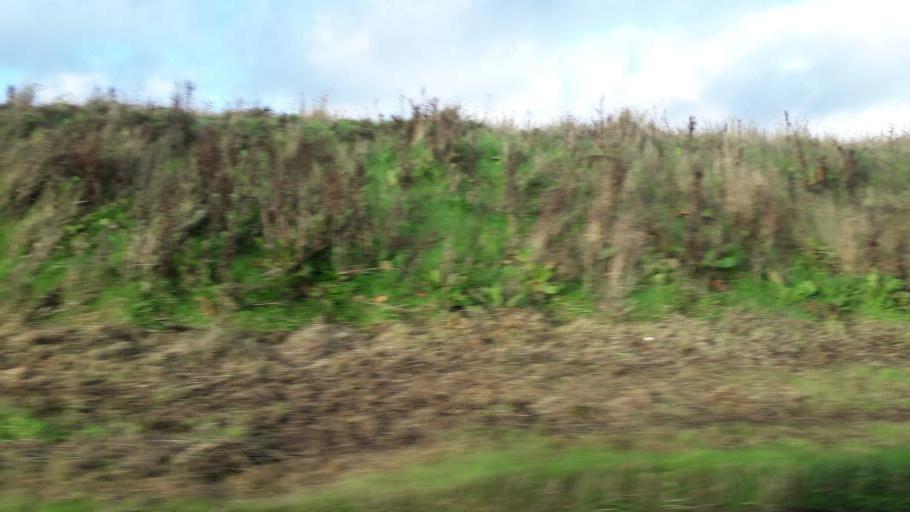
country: IE
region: Connaught
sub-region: Roscommon
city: Ballaghaderreen
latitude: 53.8889
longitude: -8.4905
